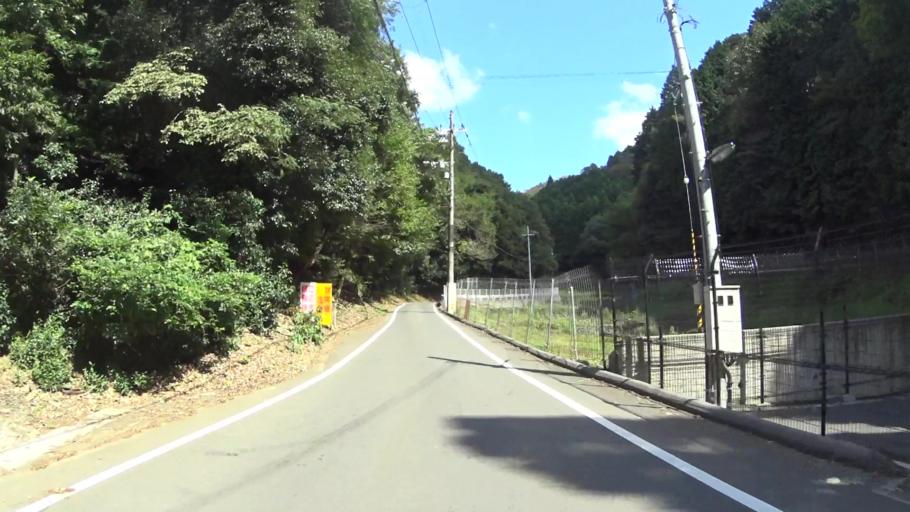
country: JP
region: Kyoto
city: Uji
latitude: 34.9159
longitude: 135.8435
